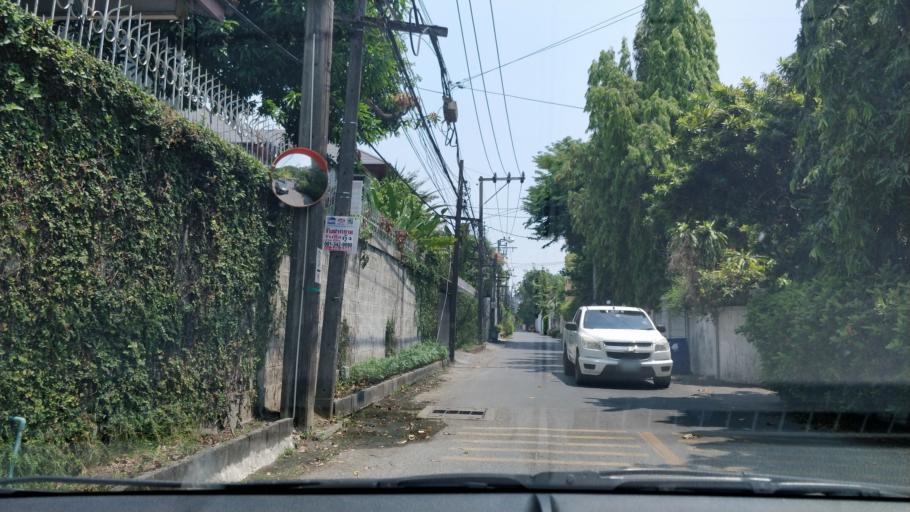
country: TH
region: Bangkok
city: Watthana
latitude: 13.7282
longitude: 100.6032
